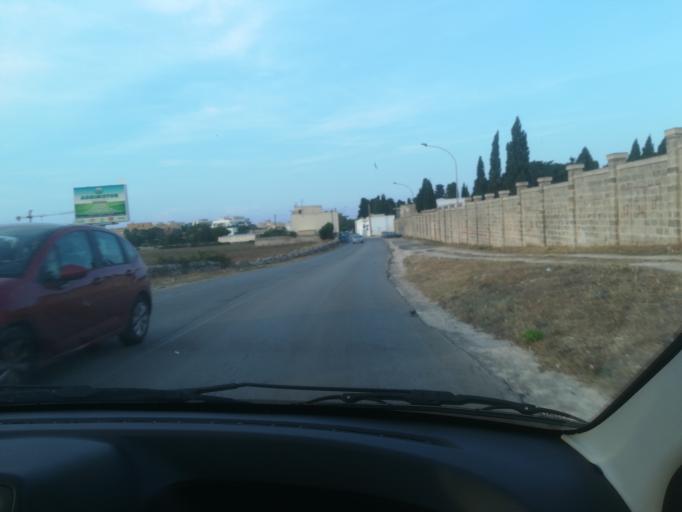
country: IT
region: Apulia
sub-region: Provincia di Bari
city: Monopoli
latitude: 40.9417
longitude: 17.2971
